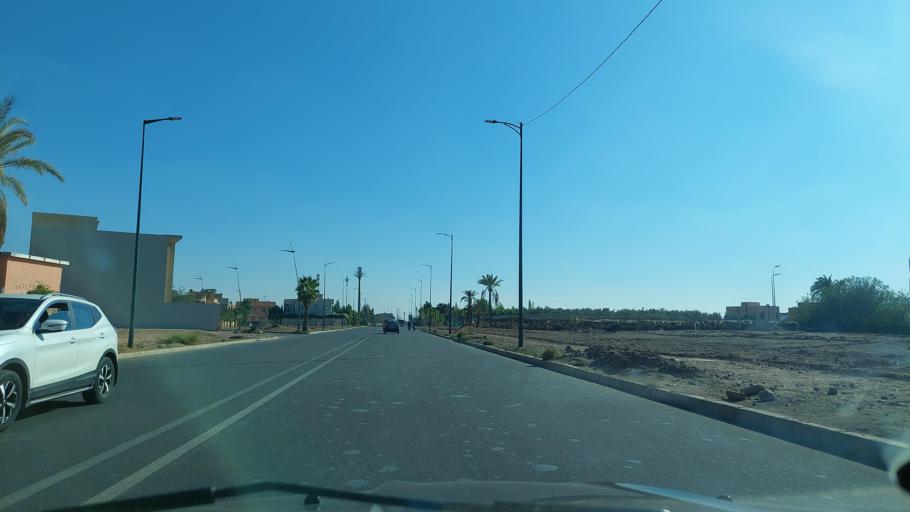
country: MA
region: Marrakech-Tensift-Al Haouz
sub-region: Marrakech
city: Marrakesh
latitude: 31.6563
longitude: -8.0663
